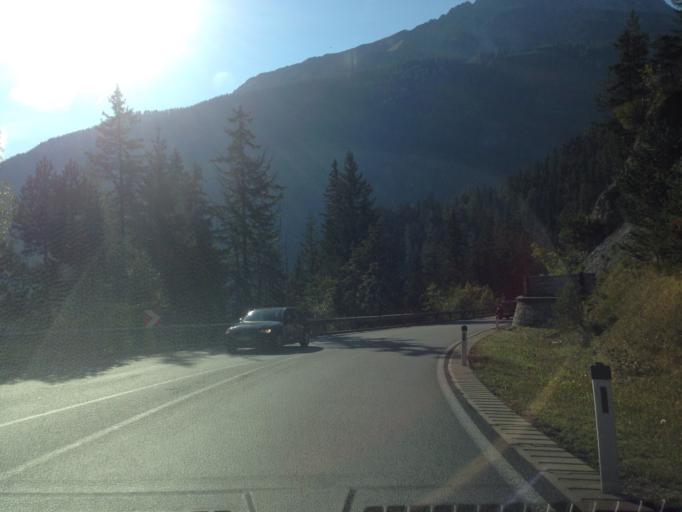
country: AT
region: Tyrol
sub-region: Politischer Bezirk Imst
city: Nassereith
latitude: 47.3611
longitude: 10.8446
